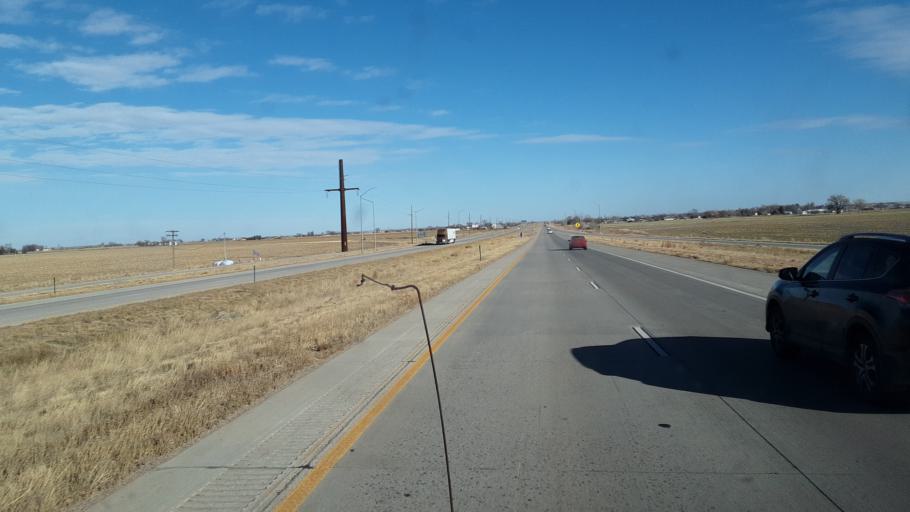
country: US
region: Colorado
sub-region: Morgan County
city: Brush
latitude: 40.2679
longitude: -103.6955
